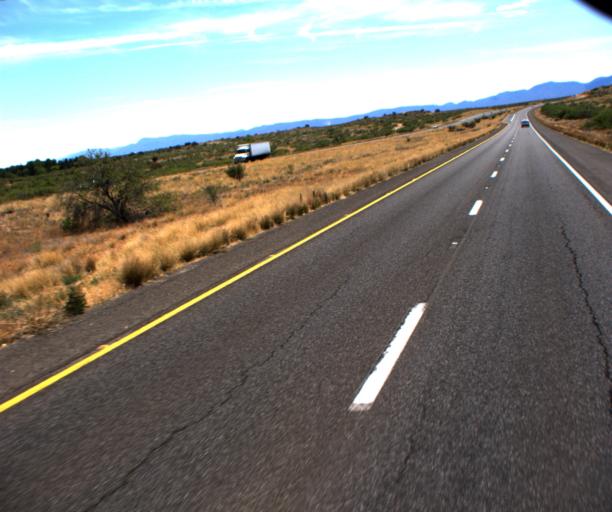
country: US
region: Arizona
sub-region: Yavapai County
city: Cornville
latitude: 34.7817
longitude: -111.9263
